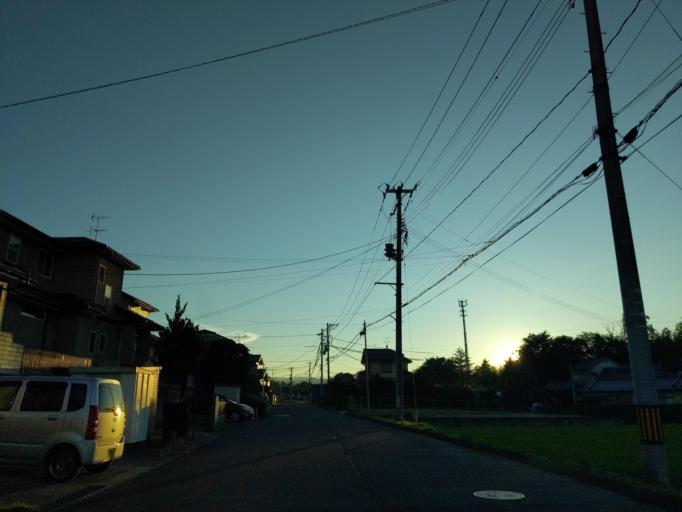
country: JP
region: Fukushima
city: Koriyama
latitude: 37.4129
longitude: 140.3311
